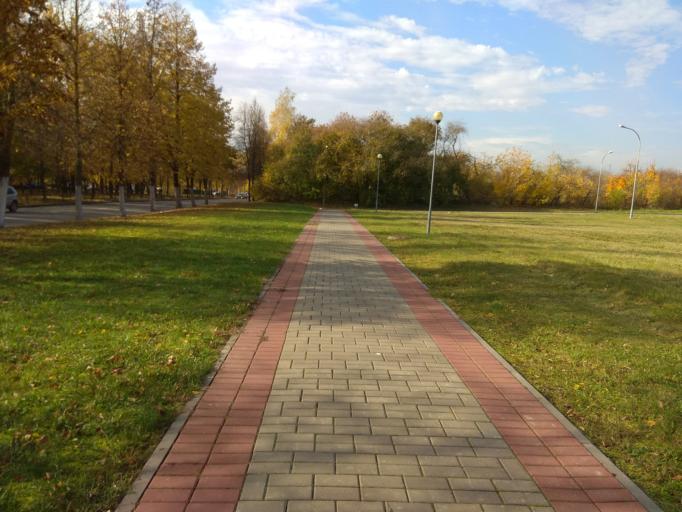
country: BY
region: Grodnenskaya
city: Hrodna
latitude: 53.7093
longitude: 23.7992
